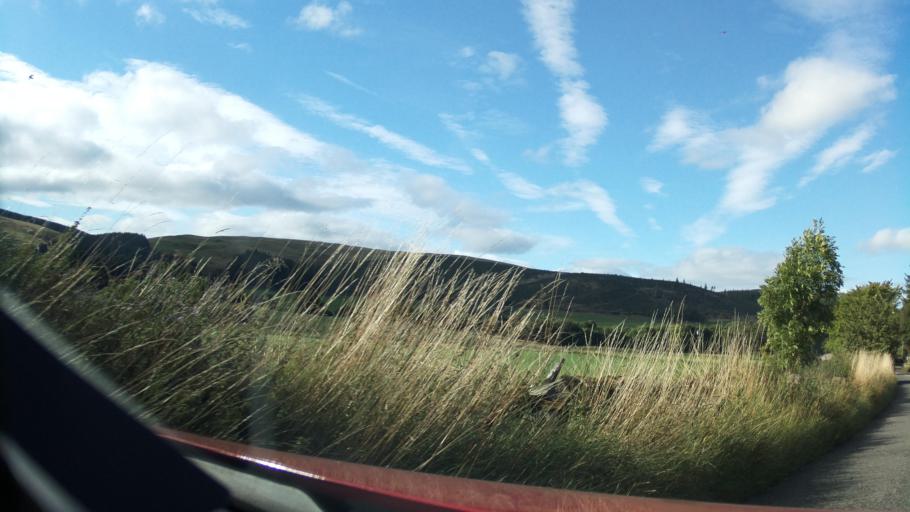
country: GB
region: Scotland
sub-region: South Lanarkshire
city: Biggar
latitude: 55.5903
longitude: -3.4046
